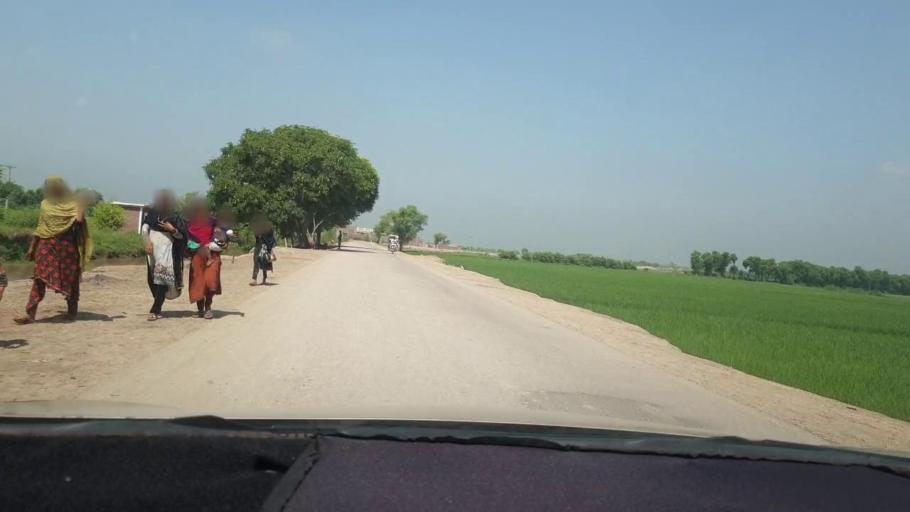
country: PK
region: Sindh
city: Miro Khan
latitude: 27.7720
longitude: 68.0608
